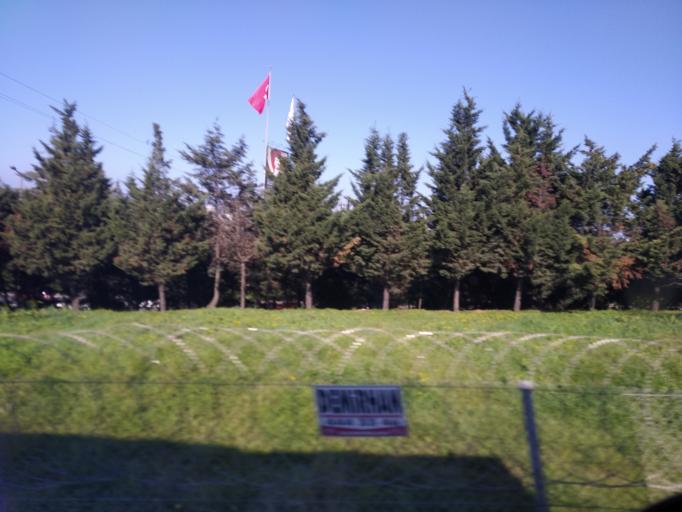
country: TR
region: Istanbul
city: Umraniye
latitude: 40.9930
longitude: 29.1678
